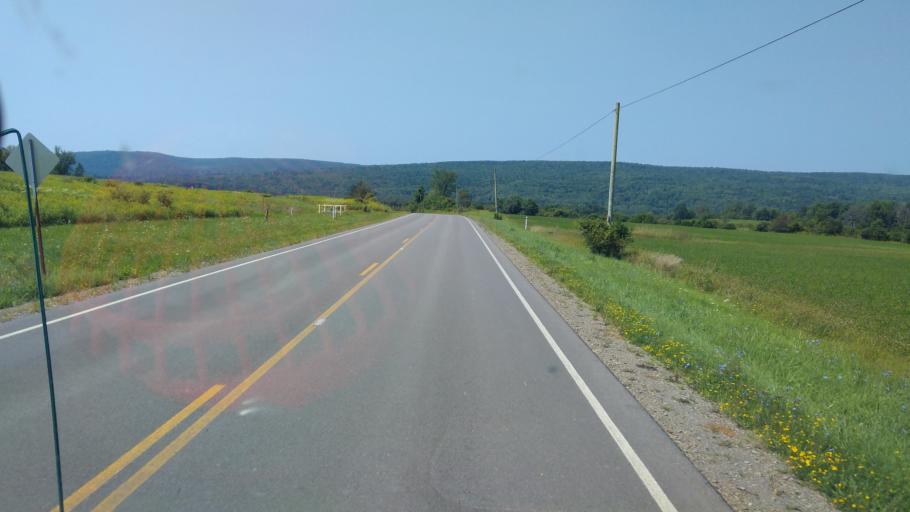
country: US
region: New York
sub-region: Allegany County
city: Belmont
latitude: 42.2716
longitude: -78.0452
